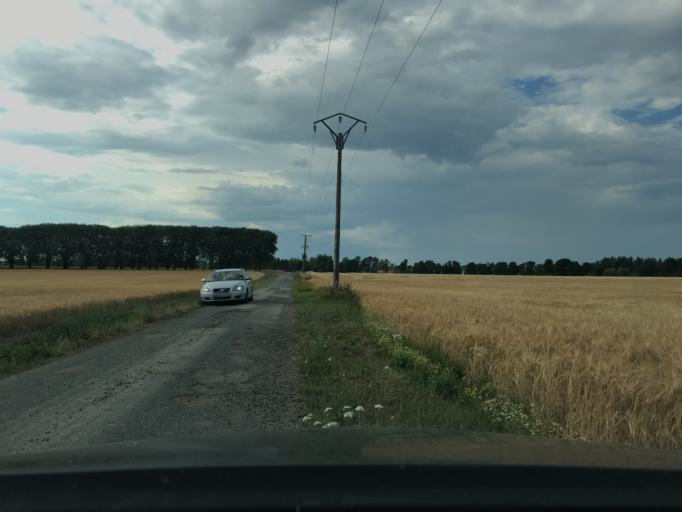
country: SE
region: Skane
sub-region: Simrishamns Kommun
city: Kivik
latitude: 55.5367
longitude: 14.1551
